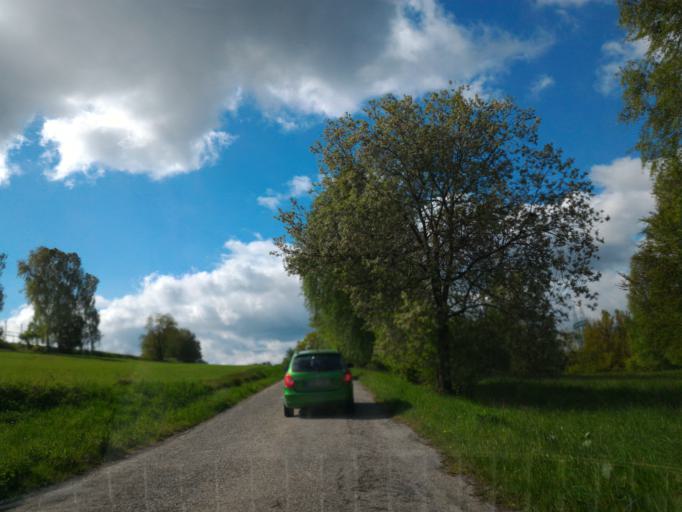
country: CZ
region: Vysocina
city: Ledec nad Sazavou
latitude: 49.6291
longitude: 15.3081
